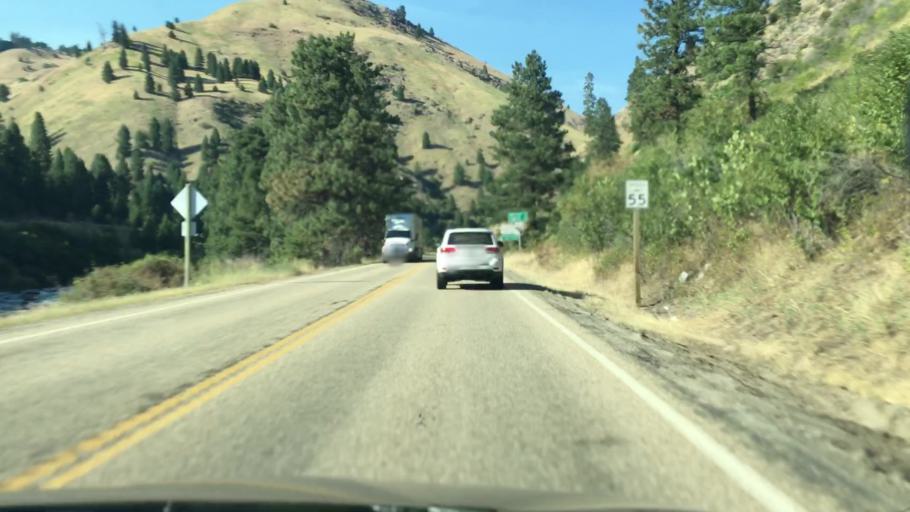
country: US
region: Idaho
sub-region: Boise County
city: Idaho City
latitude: 44.0857
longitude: -116.1140
